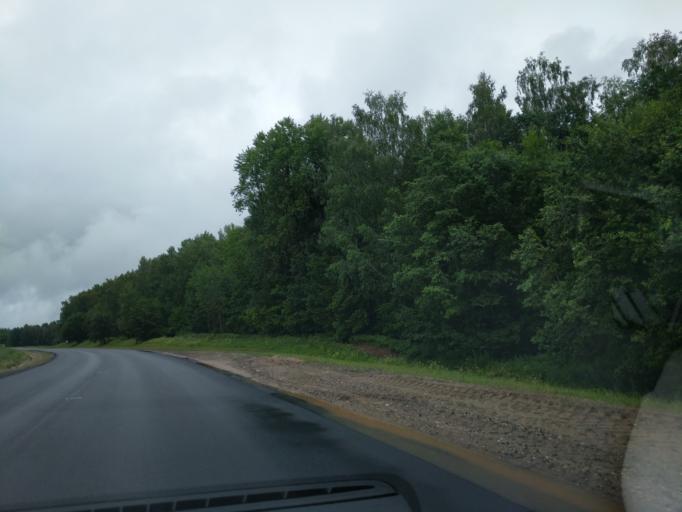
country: BY
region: Minsk
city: Syomkava
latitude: 54.2514
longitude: 27.4898
